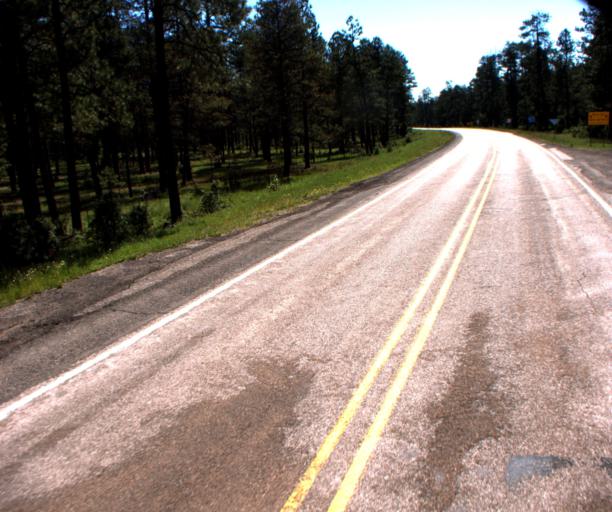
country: US
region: New Mexico
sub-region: Catron County
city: Reserve
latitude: 33.8107
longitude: -109.0468
